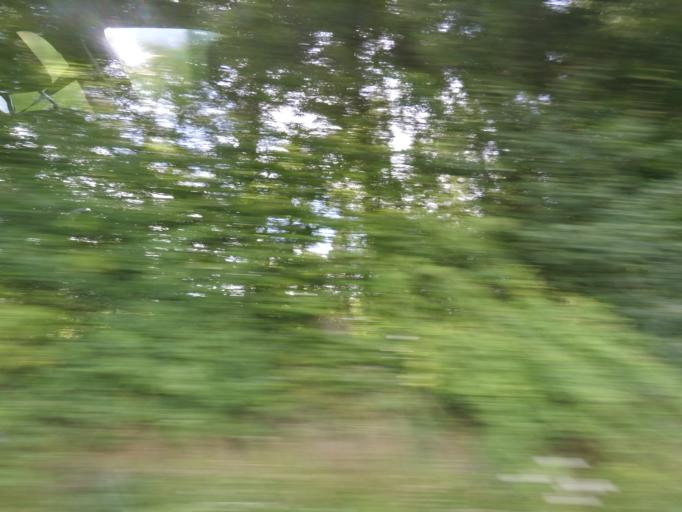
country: DK
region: South Denmark
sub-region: Assens Kommune
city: Vissenbjerg
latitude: 55.4144
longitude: 10.1755
